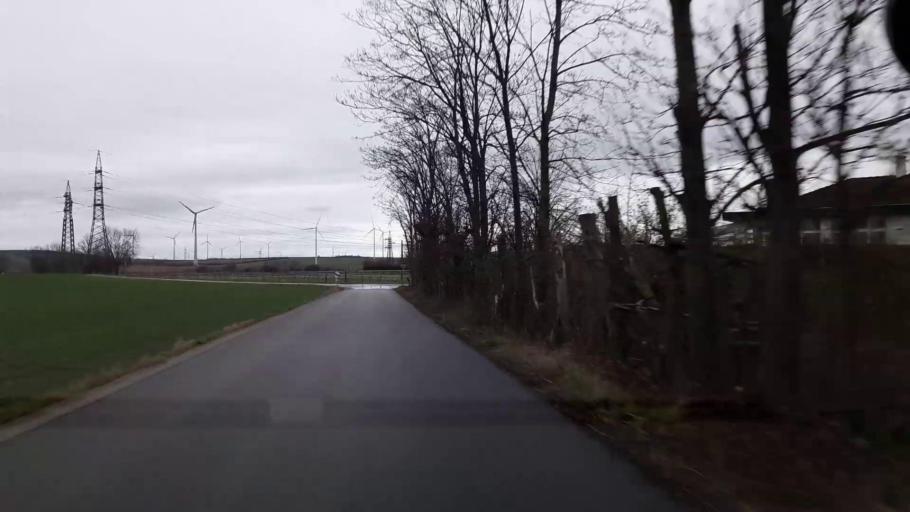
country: AT
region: Lower Austria
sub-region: Politischer Bezirk Bruck an der Leitha
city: Bruck an der Leitha
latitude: 48.0311
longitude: 16.7655
